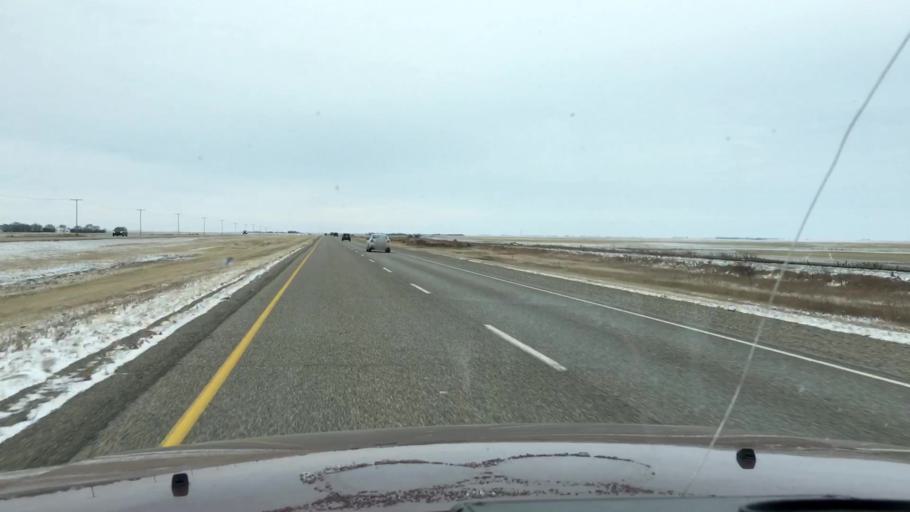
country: CA
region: Saskatchewan
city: Watrous
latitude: 51.1382
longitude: -105.9010
